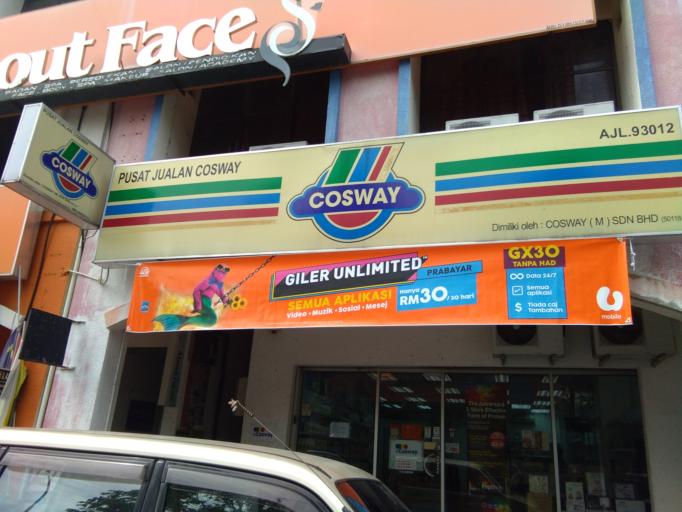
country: MY
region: Perak
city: Ipoh
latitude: 4.5988
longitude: 101.0932
